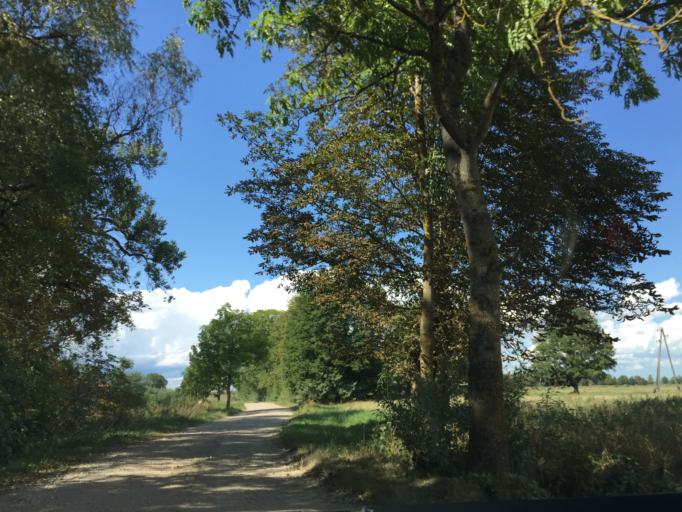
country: LT
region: Siauliu apskritis
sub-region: Joniskis
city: Joniskis
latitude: 56.3416
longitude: 23.5538
